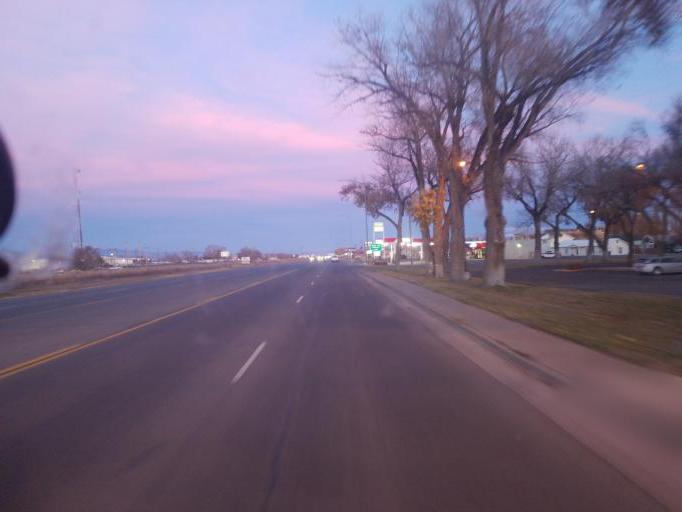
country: US
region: Colorado
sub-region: Alamosa County
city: Alamosa
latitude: 37.4691
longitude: -105.8799
